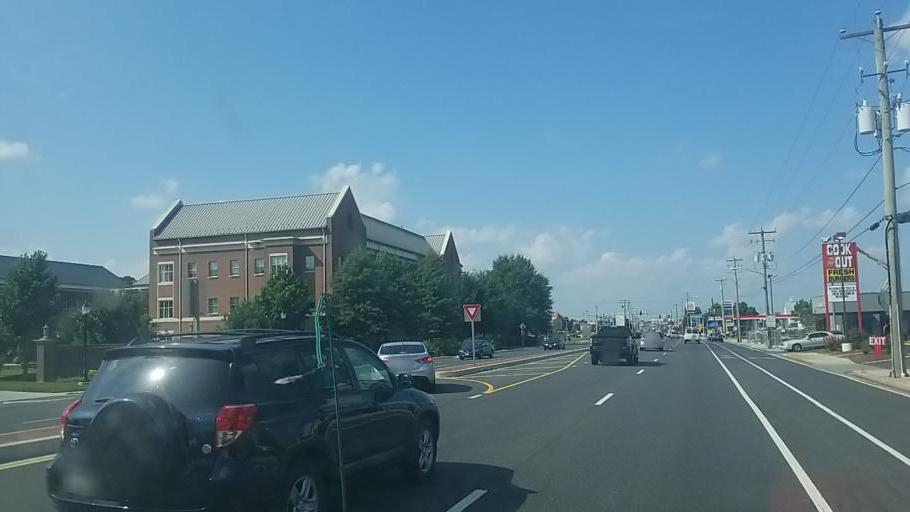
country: US
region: Maryland
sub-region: Wicomico County
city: Salisbury
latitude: 38.3470
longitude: -75.6026
